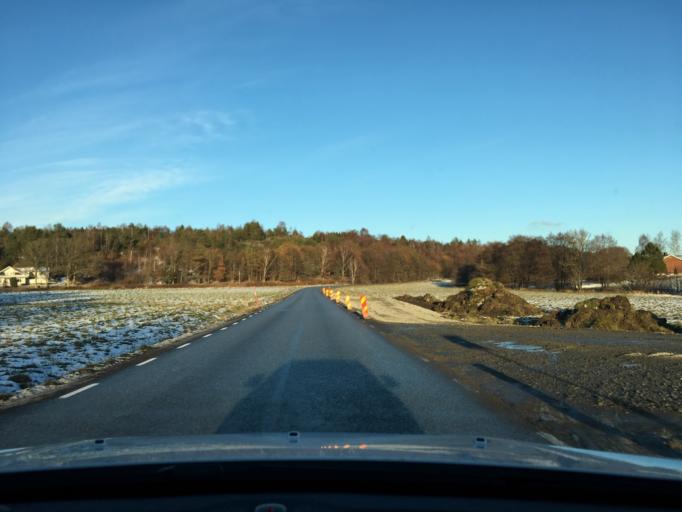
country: SE
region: Vaestra Goetaland
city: Svanesund
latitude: 58.1419
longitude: 11.7922
